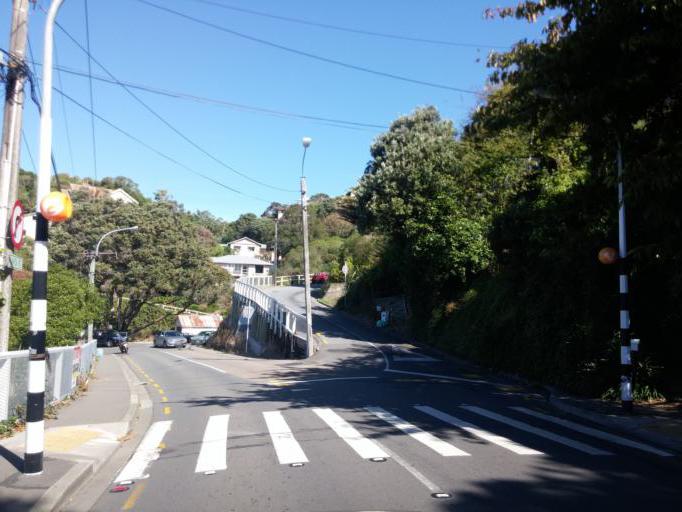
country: NZ
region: Wellington
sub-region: Wellington City
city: Kelburn
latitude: -41.2898
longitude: 174.7583
